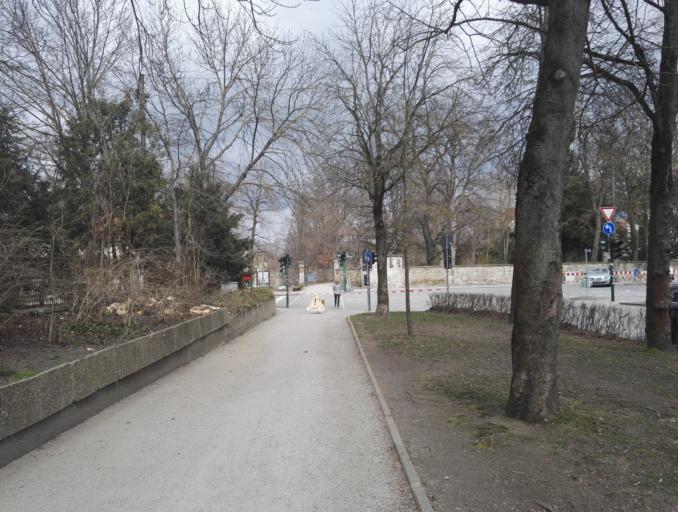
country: DE
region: Bavaria
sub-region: Upper Palatinate
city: Regensburg
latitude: 49.0176
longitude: 12.1082
